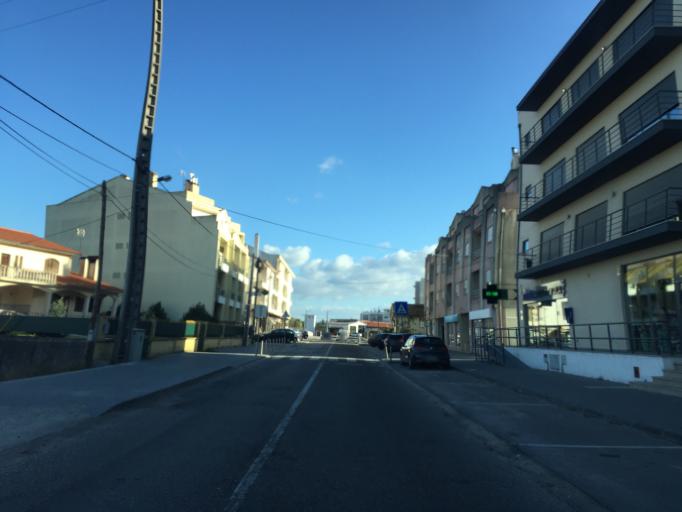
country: PT
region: Leiria
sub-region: Leiria
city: Monte Redondo
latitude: 39.9510
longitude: -8.7851
